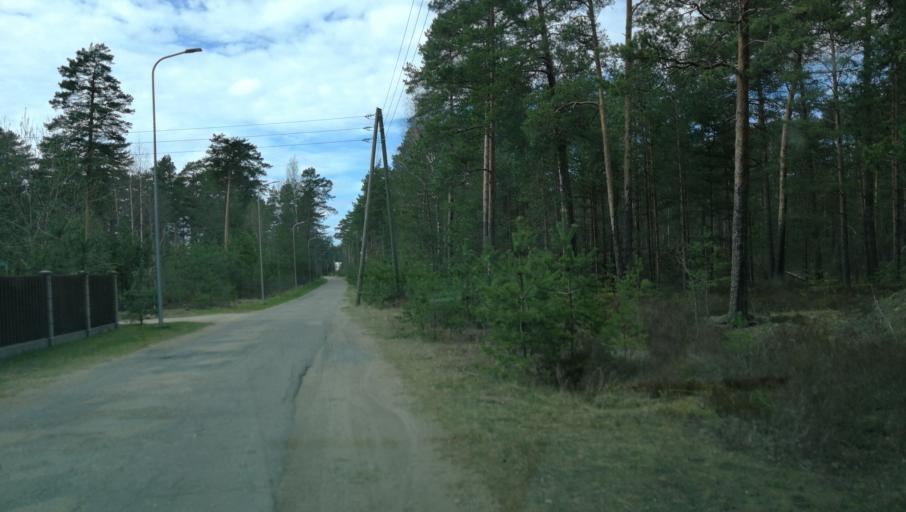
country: LV
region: Garkalne
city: Garkalne
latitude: 57.0388
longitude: 24.4400
